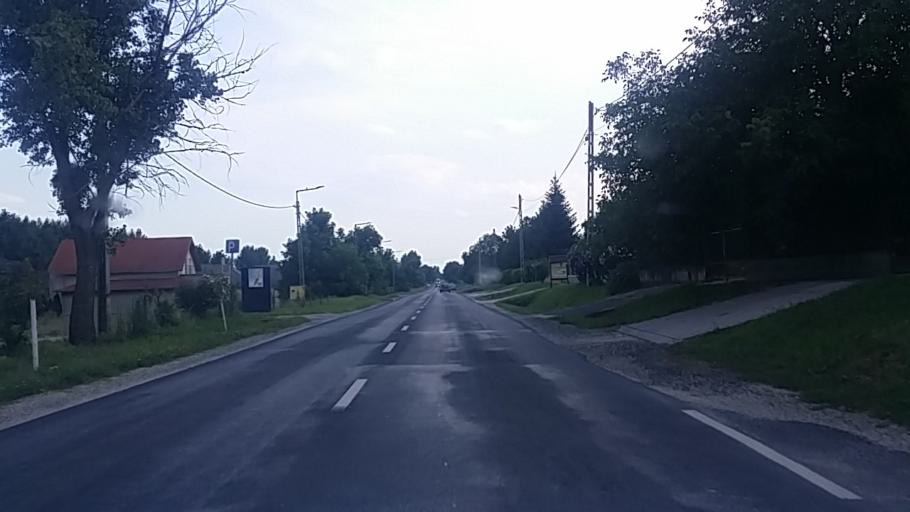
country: HU
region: Zala
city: Heviz
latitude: 46.7549
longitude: 17.1749
